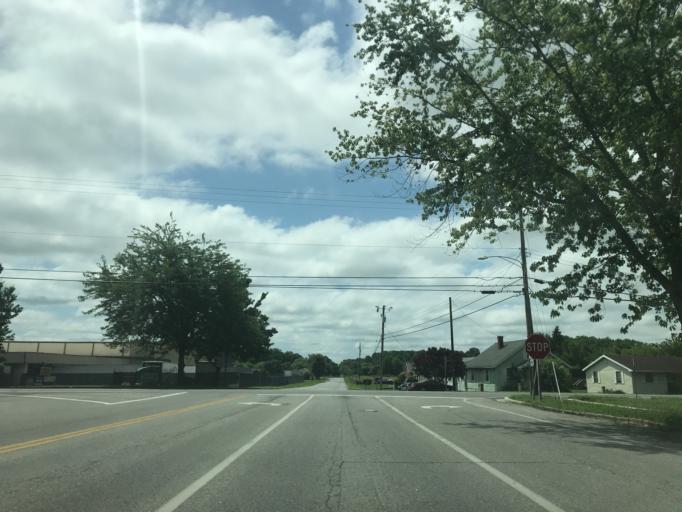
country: US
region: Maryland
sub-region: Caroline County
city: Ridgely
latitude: 38.9425
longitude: -75.8812
